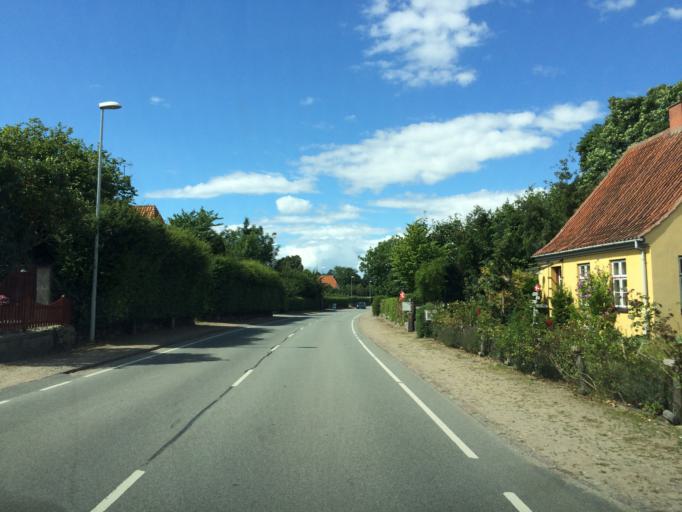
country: DK
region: South Denmark
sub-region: Faaborg-Midtfyn Kommune
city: Faaborg
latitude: 55.1334
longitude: 10.2035
